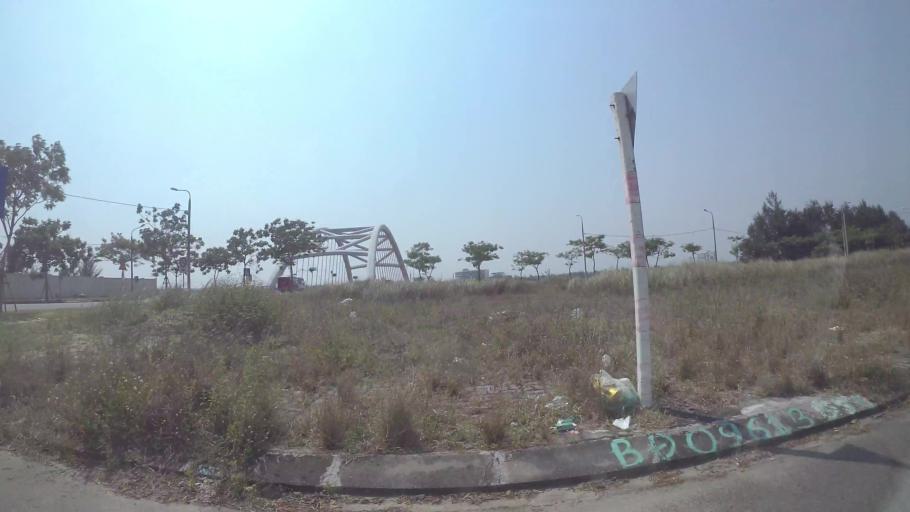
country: VN
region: Da Nang
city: Ngu Hanh Son
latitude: 15.9785
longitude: 108.2696
